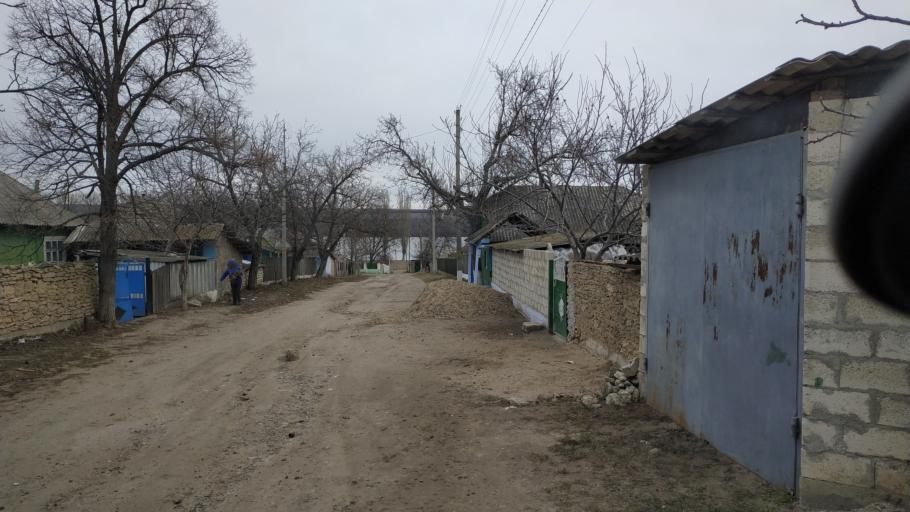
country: MD
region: Telenesti
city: Cocieri
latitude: 47.3791
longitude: 29.1257
